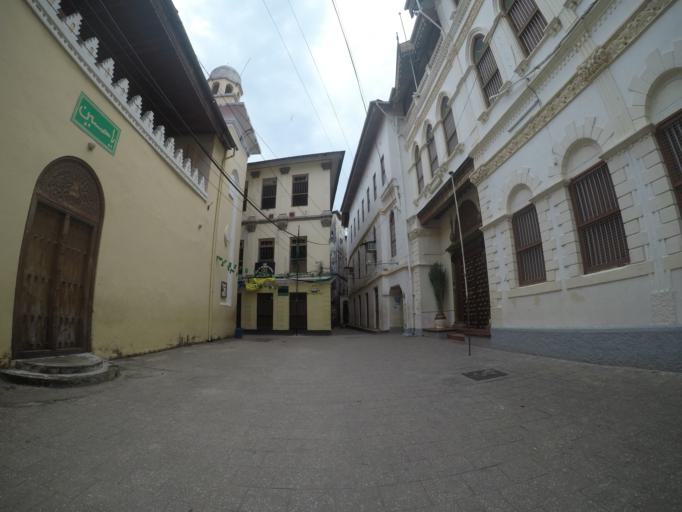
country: TZ
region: Zanzibar Urban/West
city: Zanzibar
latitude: -6.1606
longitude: 39.1918
